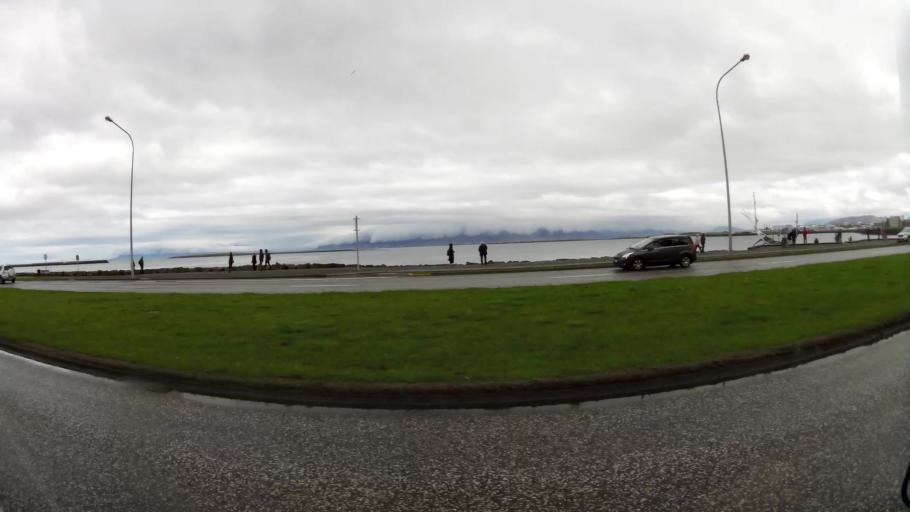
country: IS
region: Capital Region
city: Reykjavik
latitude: 64.1475
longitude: -21.9235
